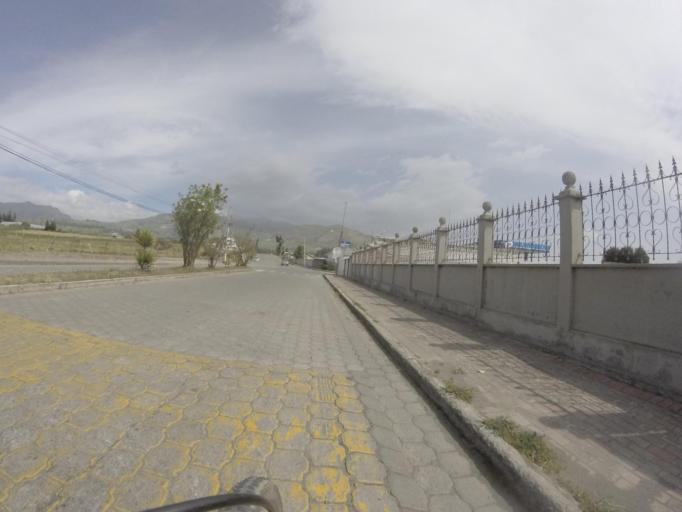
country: EC
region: Pichincha
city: Cayambe
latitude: 0.1405
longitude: -78.0742
